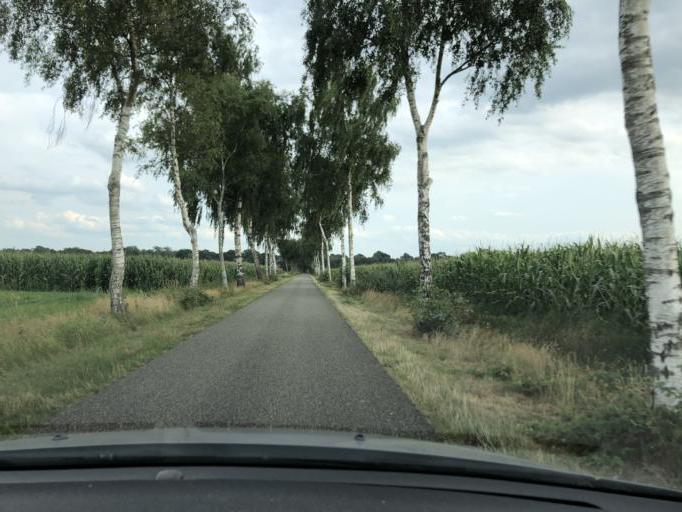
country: NL
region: Overijssel
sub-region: Gemeente Dalfsen
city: Dalfsen
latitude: 52.5856
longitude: 6.3189
